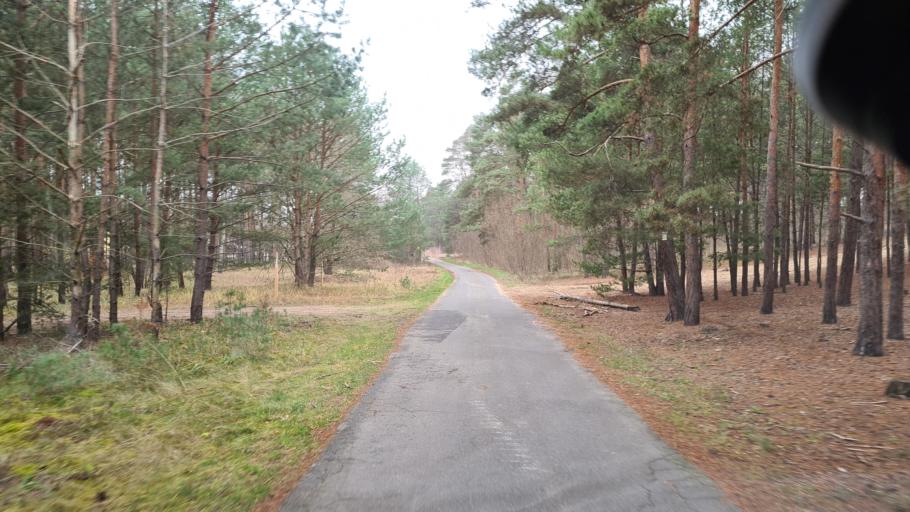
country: DE
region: Brandenburg
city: Schenkendobern
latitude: 51.9747
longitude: 14.6375
